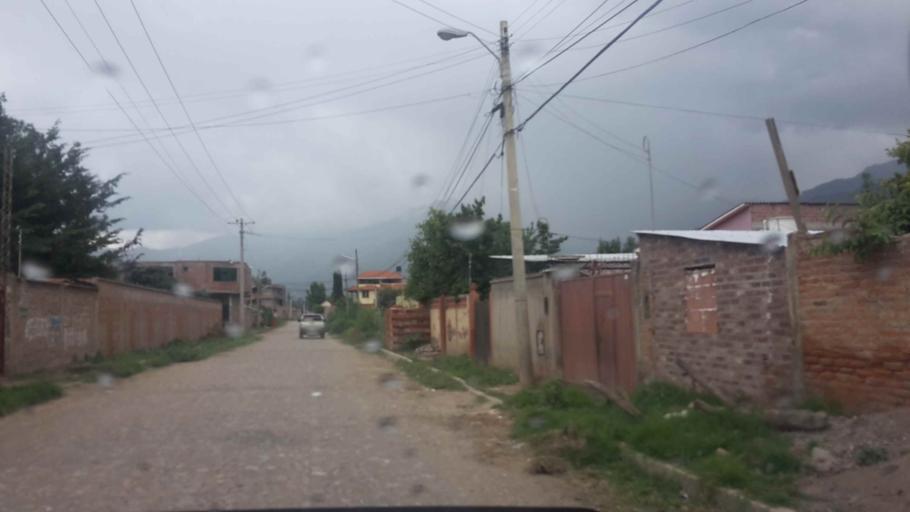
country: BO
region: Cochabamba
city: Cochabamba
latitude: -17.3391
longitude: -66.2241
